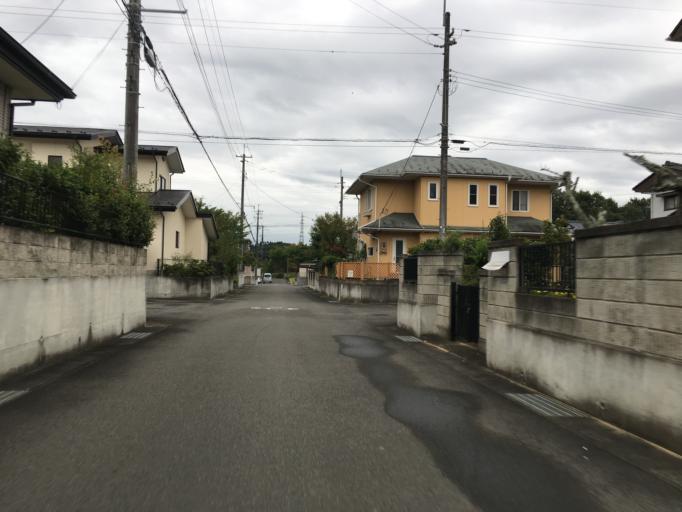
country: JP
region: Fukushima
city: Fukushima-shi
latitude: 37.6913
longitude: 140.4831
